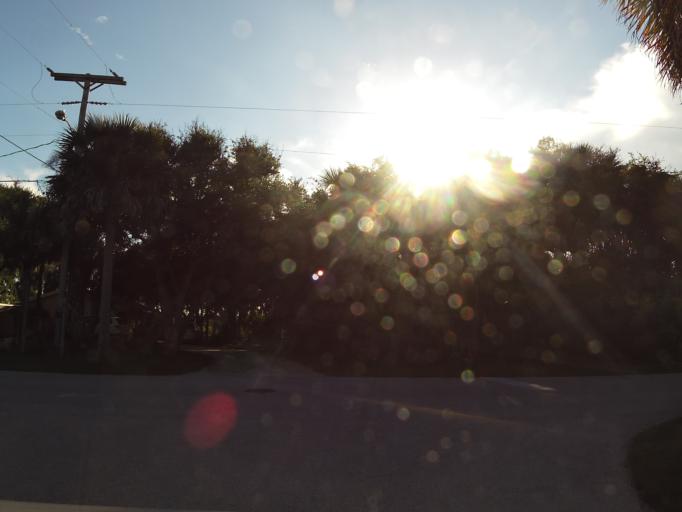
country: US
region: Florida
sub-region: Flagler County
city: Flagler Beach
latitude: 29.4679
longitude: -81.1247
